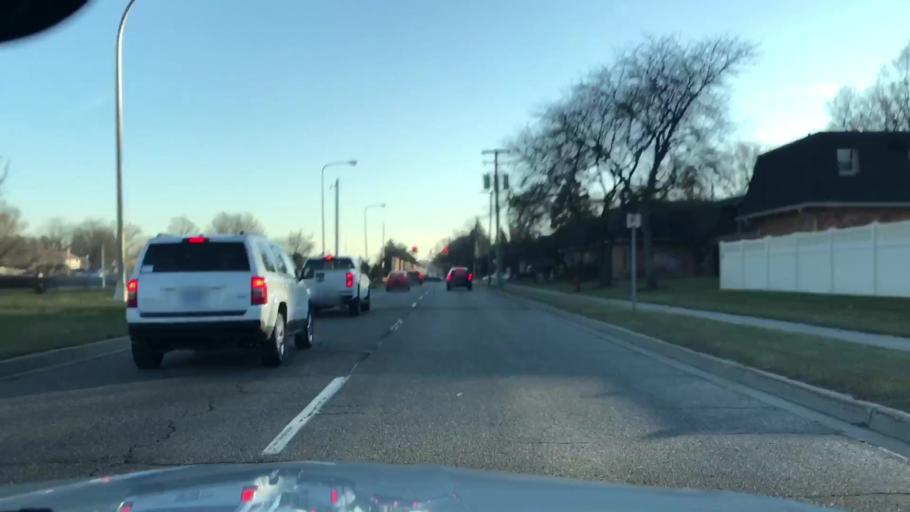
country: US
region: Michigan
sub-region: Oakland County
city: Madison Heights
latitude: 42.4997
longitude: -83.1179
